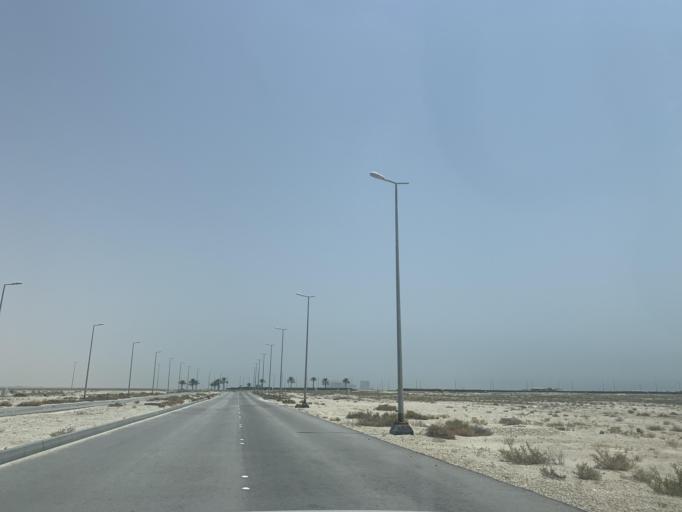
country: BH
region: Central Governorate
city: Dar Kulayb
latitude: 25.8455
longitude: 50.5904
